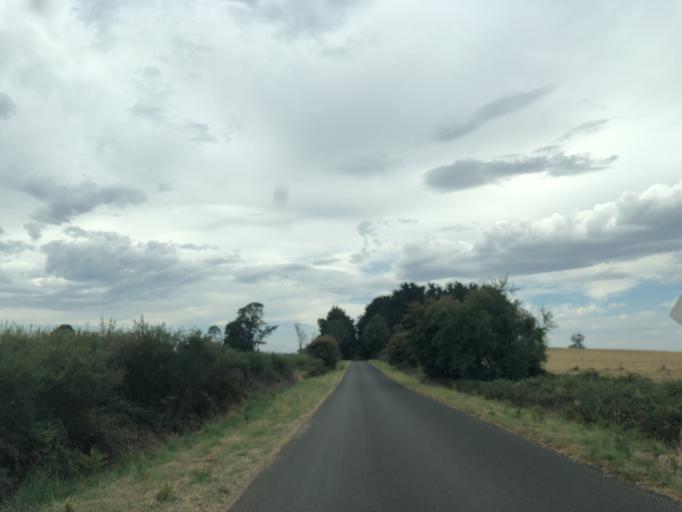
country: AU
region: Victoria
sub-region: Moorabool
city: Bacchus Marsh
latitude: -37.4044
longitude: 144.3544
